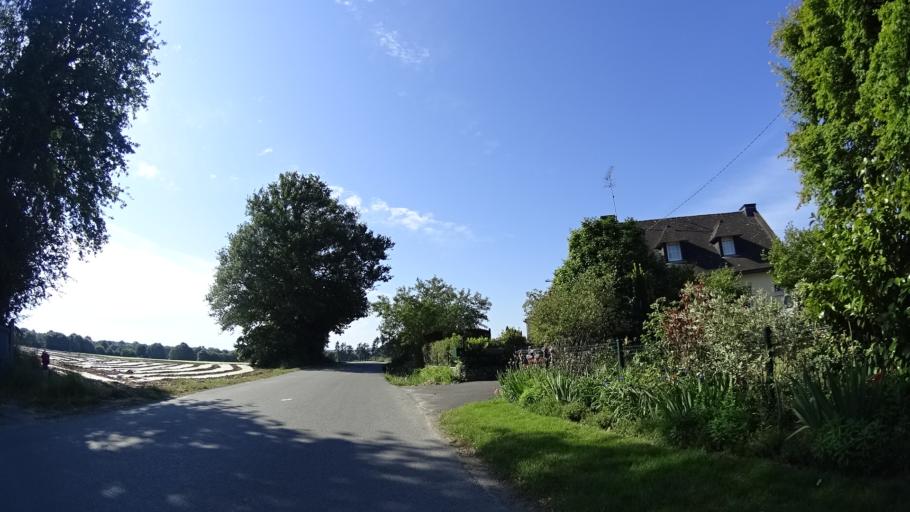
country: FR
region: Brittany
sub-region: Departement d'Ille-et-Vilaine
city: Guipry
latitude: 47.8115
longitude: -1.8506
